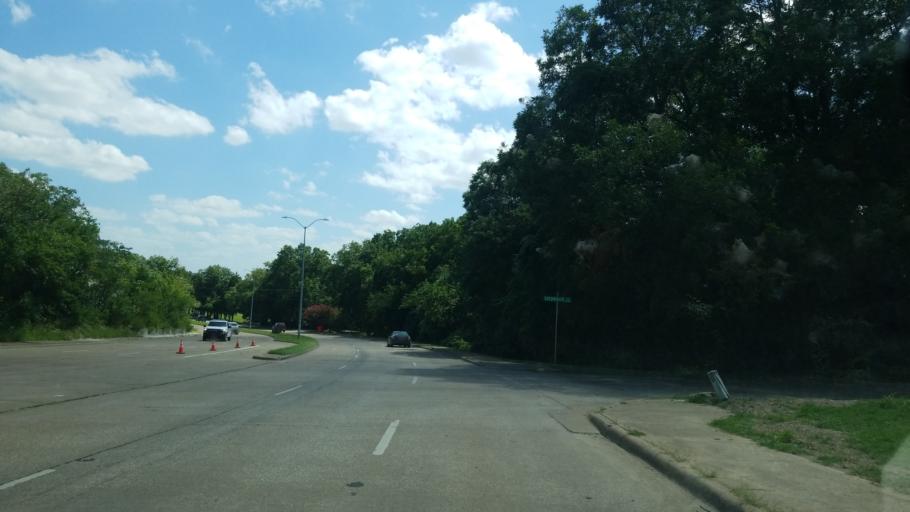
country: US
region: Texas
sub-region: Dallas County
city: Balch Springs
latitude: 32.7611
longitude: -96.7013
